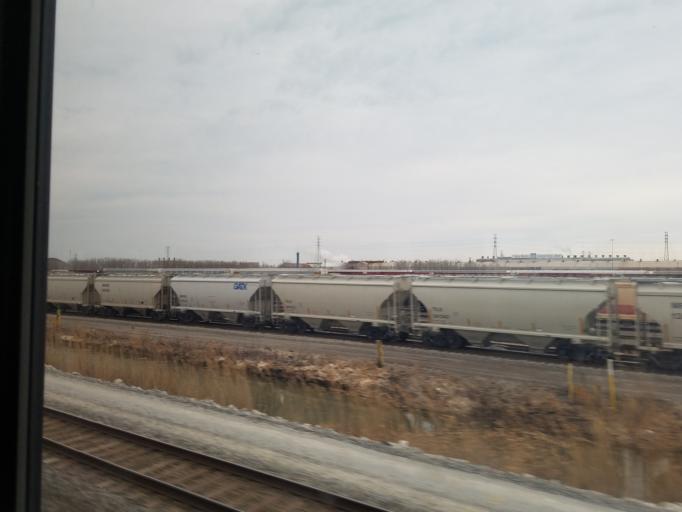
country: US
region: Indiana
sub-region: Lake County
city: Gary
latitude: 41.6061
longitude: -87.3632
